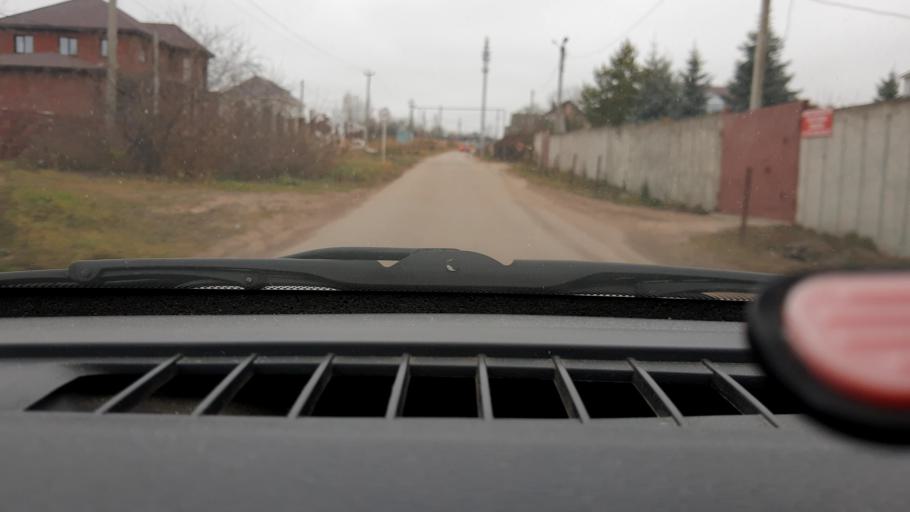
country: RU
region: Nizjnij Novgorod
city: Burevestnik
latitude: 56.1842
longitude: 43.9155
